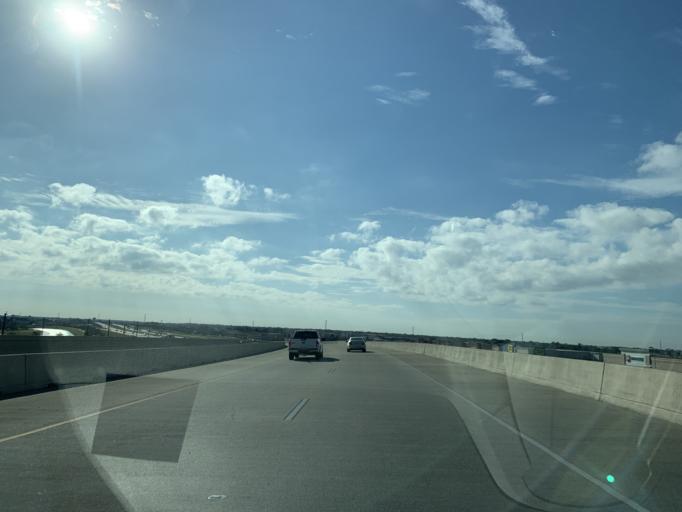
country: US
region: Texas
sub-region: Fort Bend County
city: Cinco Ranch
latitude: 29.6994
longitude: -95.7759
